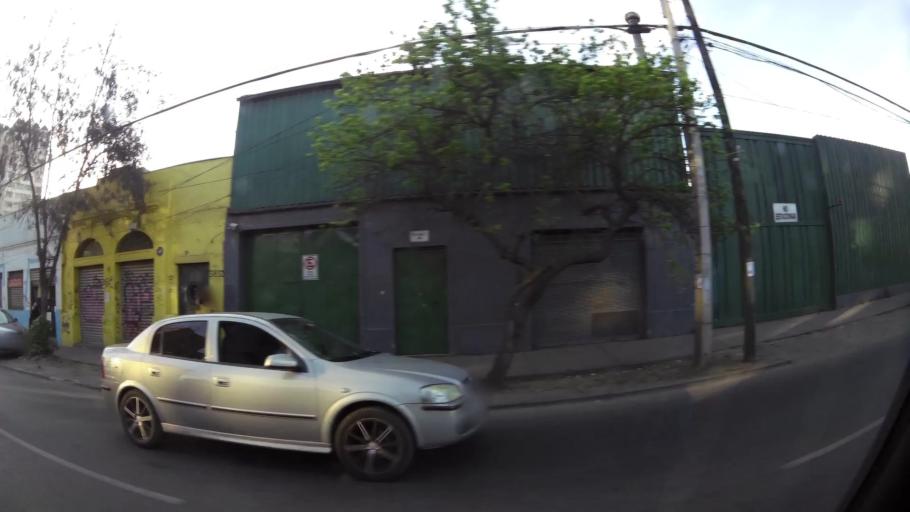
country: CL
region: Santiago Metropolitan
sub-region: Provincia de Santiago
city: Lo Prado
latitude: -33.4372
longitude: -70.6877
